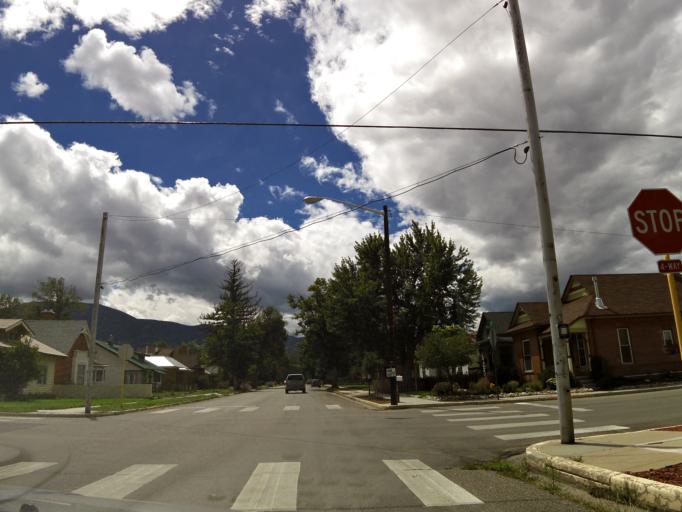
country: US
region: Colorado
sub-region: Chaffee County
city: Salida
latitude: 38.5314
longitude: -105.9967
